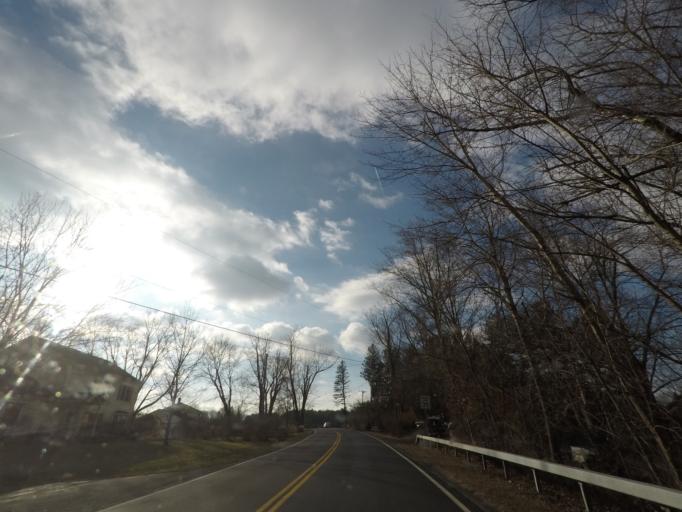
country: US
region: New York
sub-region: Albany County
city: Westmere
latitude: 42.6640
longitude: -73.8888
